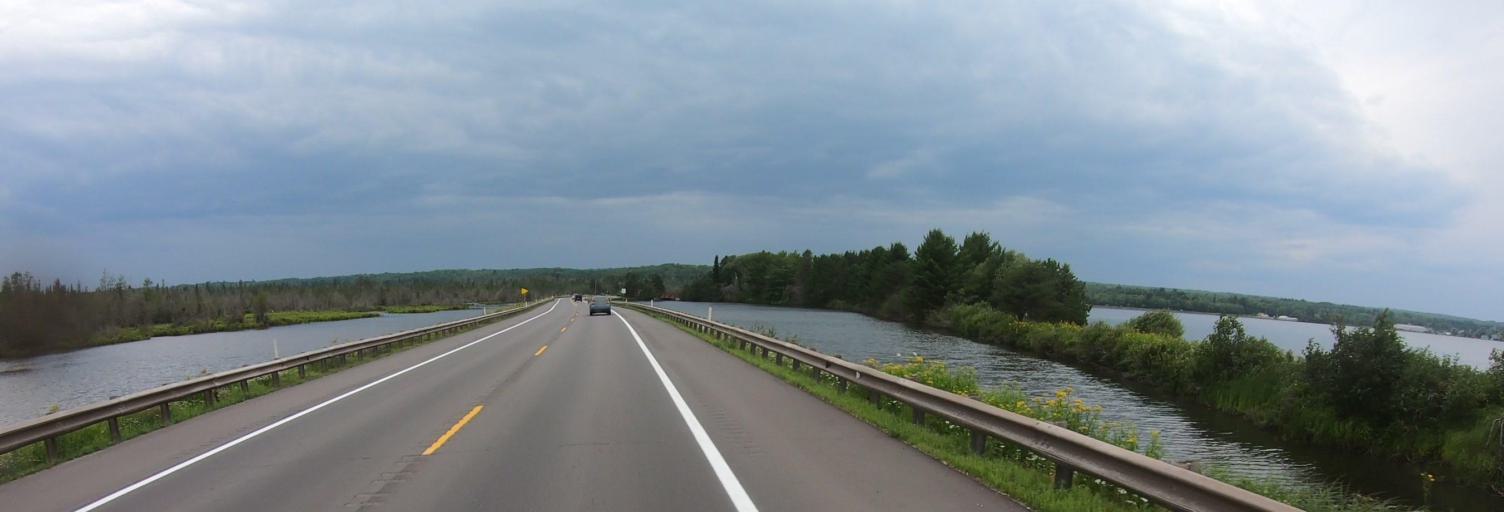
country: US
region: Michigan
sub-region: Baraga County
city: Baraga
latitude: 46.7538
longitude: -88.4888
